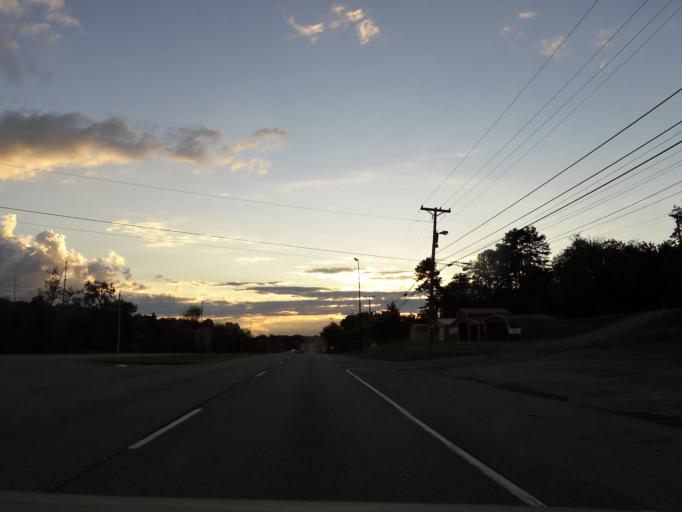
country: US
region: Tennessee
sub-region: Knox County
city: Mascot
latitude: 36.0199
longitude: -83.7947
